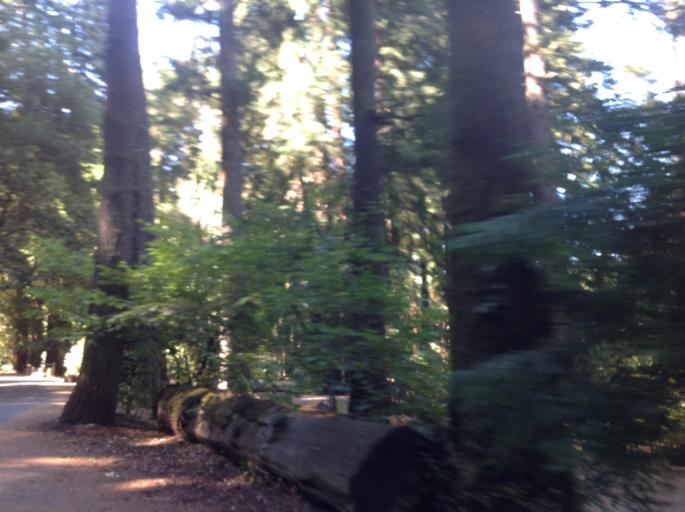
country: US
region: California
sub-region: Marin County
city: Lagunitas-Forest Knolls
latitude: 38.0218
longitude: -122.7352
